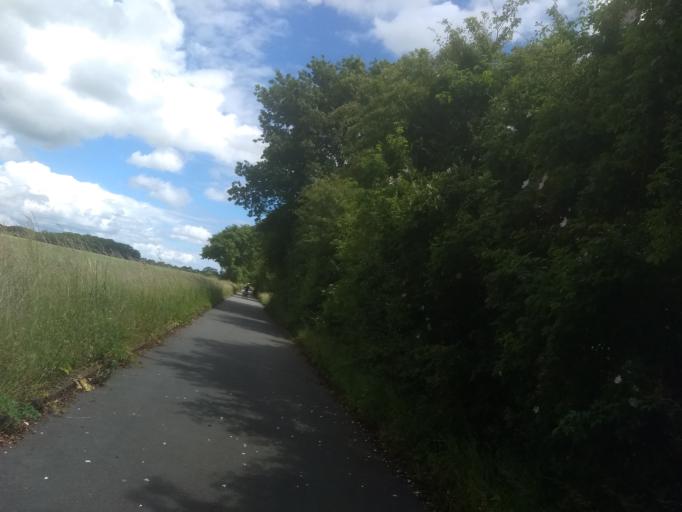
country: FR
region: Nord-Pas-de-Calais
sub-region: Departement du Pas-de-Calais
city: Beaumetz-les-Loges
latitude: 50.2314
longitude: 2.6371
